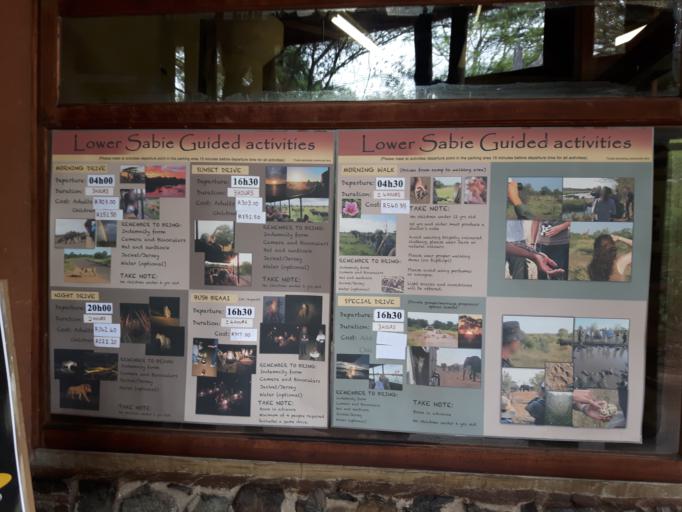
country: ZA
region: Mpumalanga
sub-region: Ehlanzeni District
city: Komatipoort
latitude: -25.1193
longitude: 31.9161
